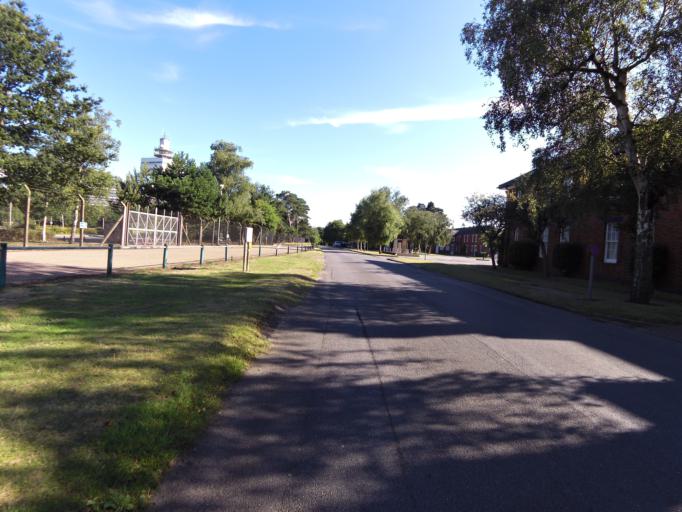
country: GB
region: England
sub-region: Suffolk
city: Kesgrave
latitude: 52.0583
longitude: 1.2782
